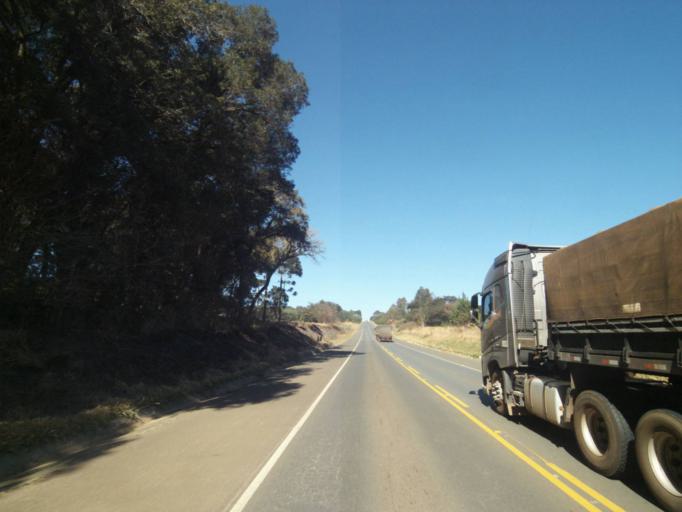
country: BR
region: Parana
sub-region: Tibagi
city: Tibagi
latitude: -24.5892
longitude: -50.4369
